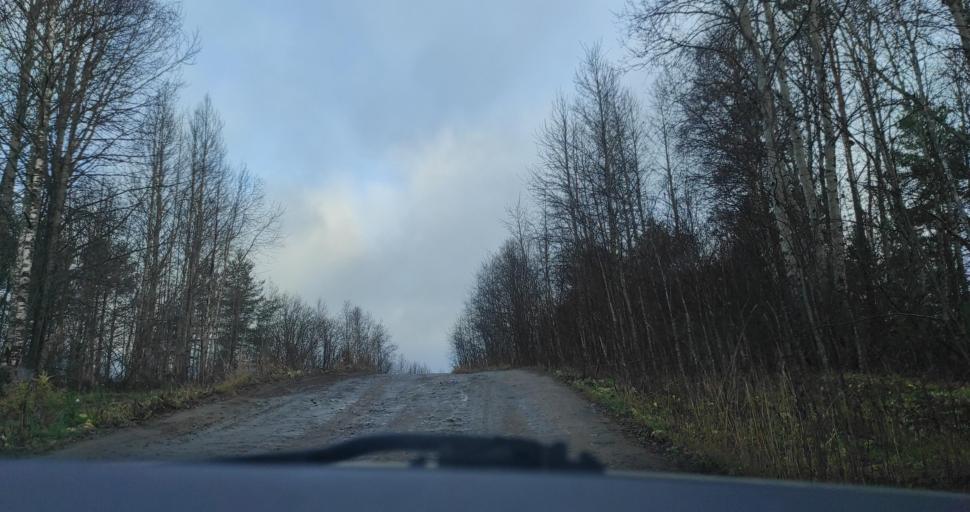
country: RU
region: Republic of Karelia
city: Pitkyaranta
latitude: 61.7320
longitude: 31.3864
